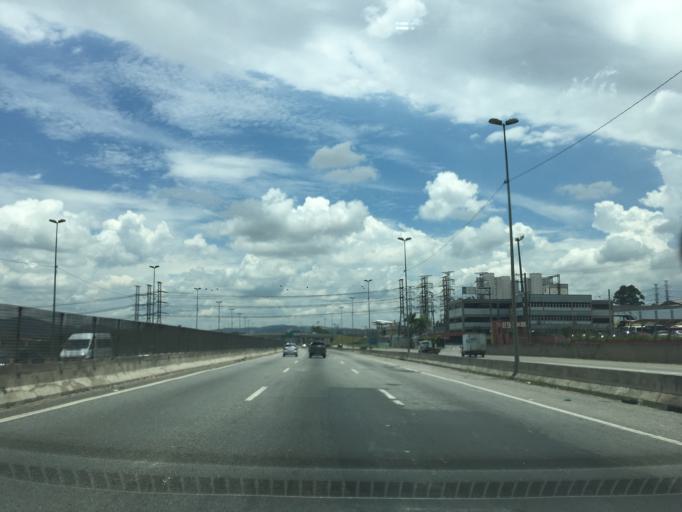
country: BR
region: Sao Paulo
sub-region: Guarulhos
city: Guarulhos
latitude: -23.4909
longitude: -46.5593
